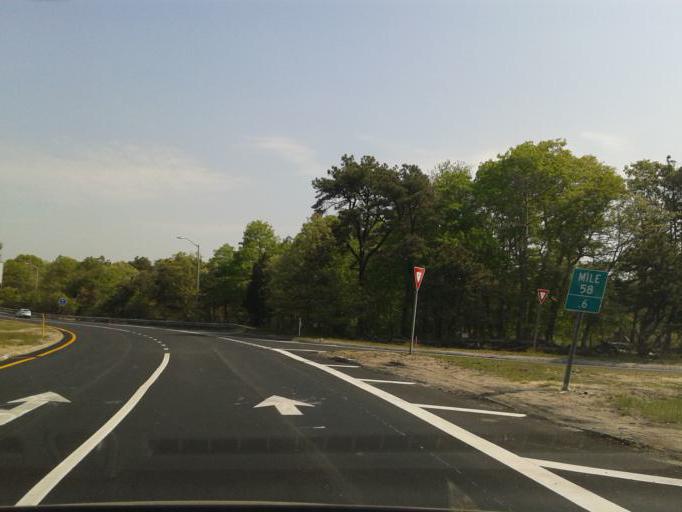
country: US
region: Massachusetts
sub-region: Barnstable County
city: Pocasset
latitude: 41.6850
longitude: -70.5904
